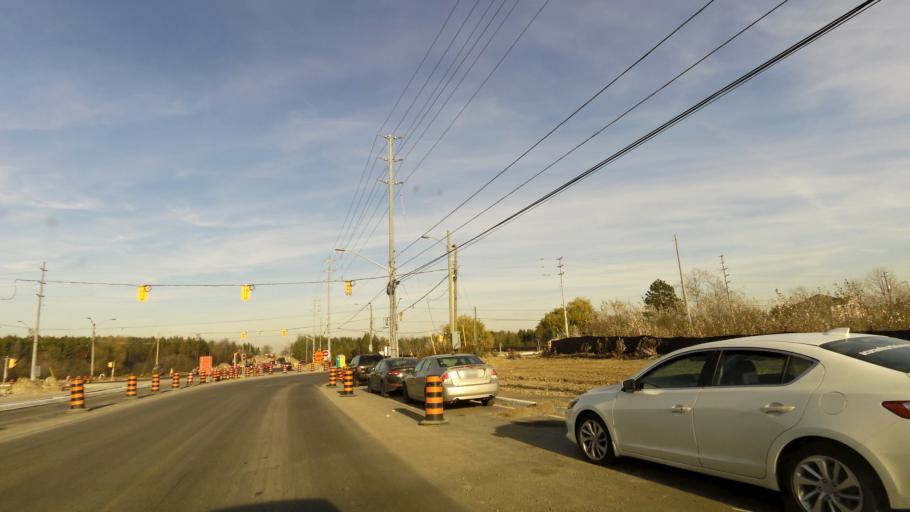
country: CA
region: Ontario
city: Brampton
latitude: 43.7921
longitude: -79.7384
